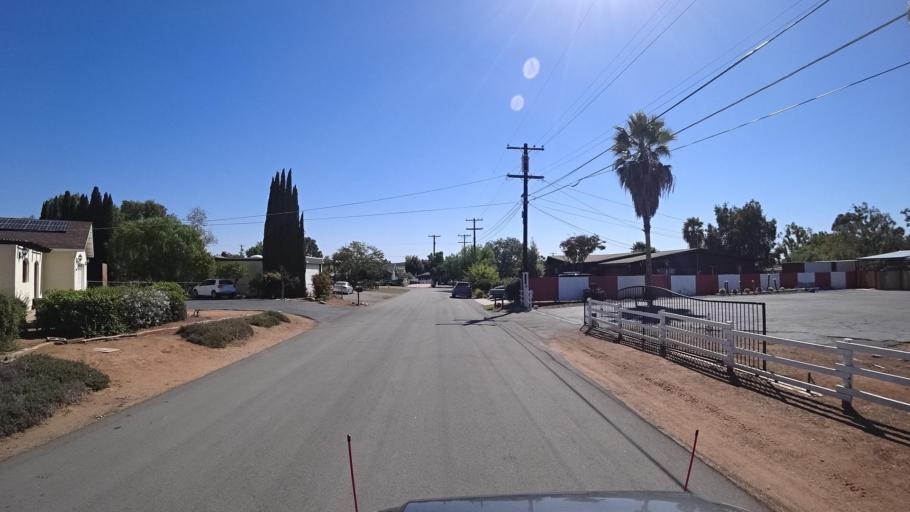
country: US
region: California
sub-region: San Diego County
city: Bonita
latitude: 32.6641
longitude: -117.0480
